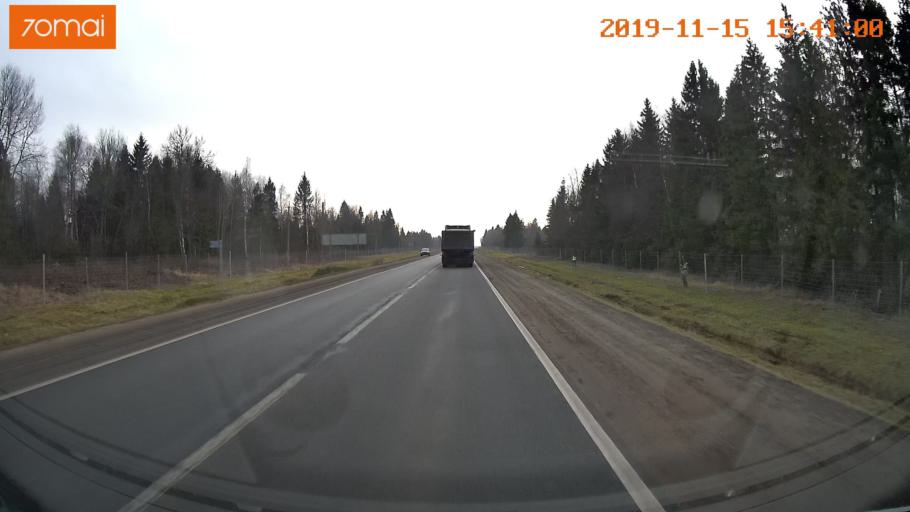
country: RU
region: Jaroslavl
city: Danilov
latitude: 58.0055
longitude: 40.0517
